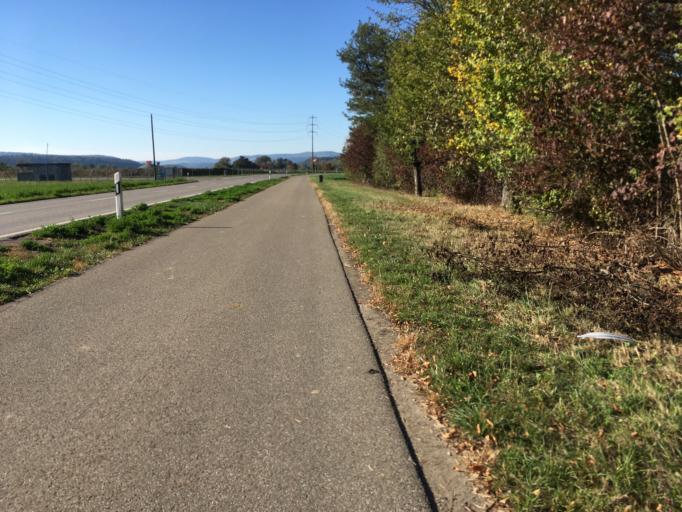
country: CH
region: Zurich
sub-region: Bezirk Buelach
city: Buelach / Soligaenter
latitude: 47.5506
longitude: 8.5351
